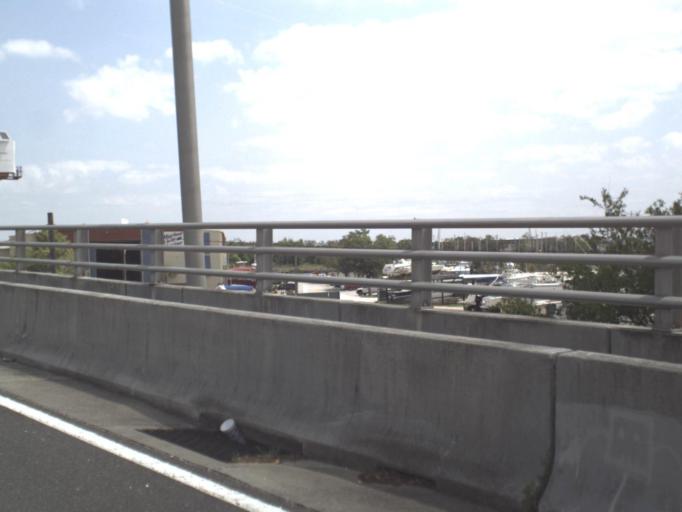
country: US
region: Florida
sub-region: Escambia County
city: Warrington
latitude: 30.3986
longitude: -87.2501
